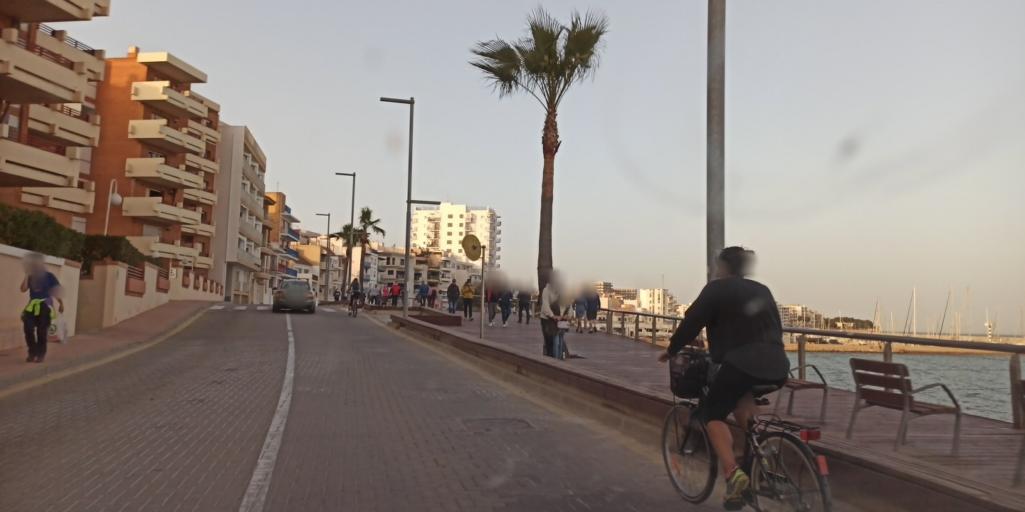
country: ES
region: Catalonia
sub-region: Provincia de Tarragona
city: L'Ampolla
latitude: 40.8089
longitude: 0.7055
